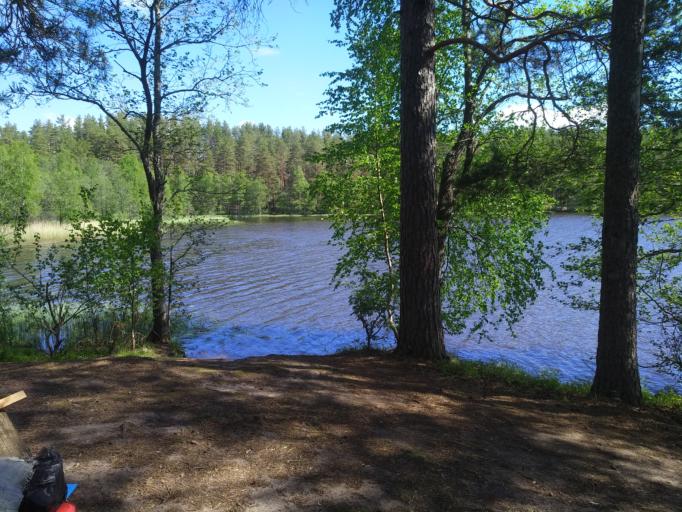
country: RU
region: Leningrad
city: Michurinskoye
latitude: 60.6017
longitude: 29.8663
